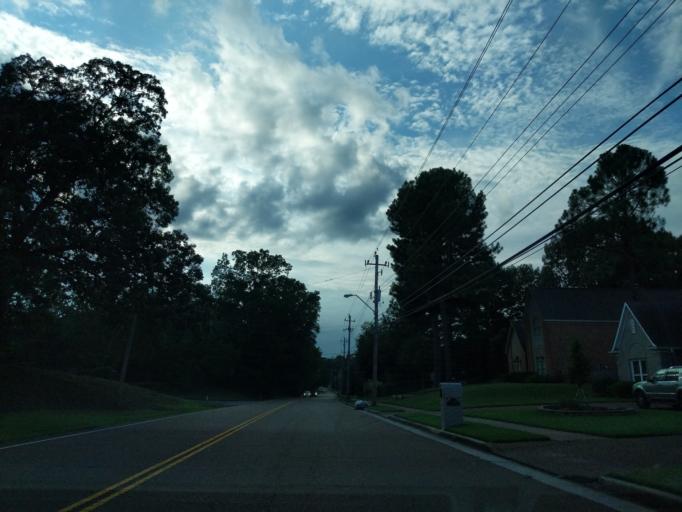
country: US
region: Tennessee
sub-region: Shelby County
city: Germantown
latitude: 35.0678
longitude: -89.7724
